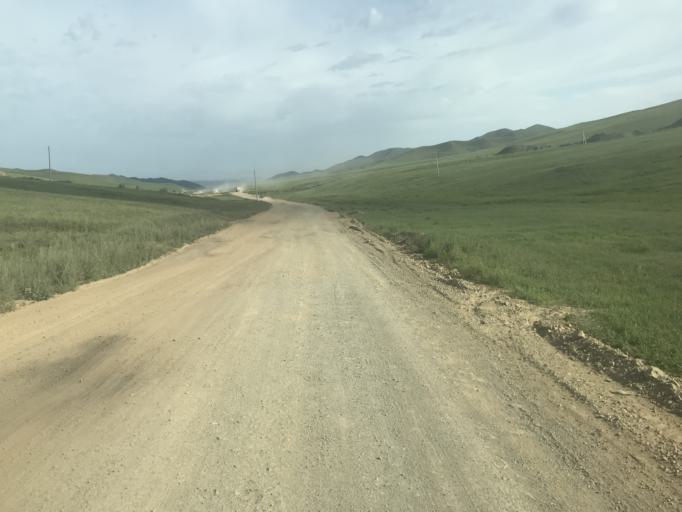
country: MN
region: Central Aimak
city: Javhlant
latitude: 48.7334
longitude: 106.1331
